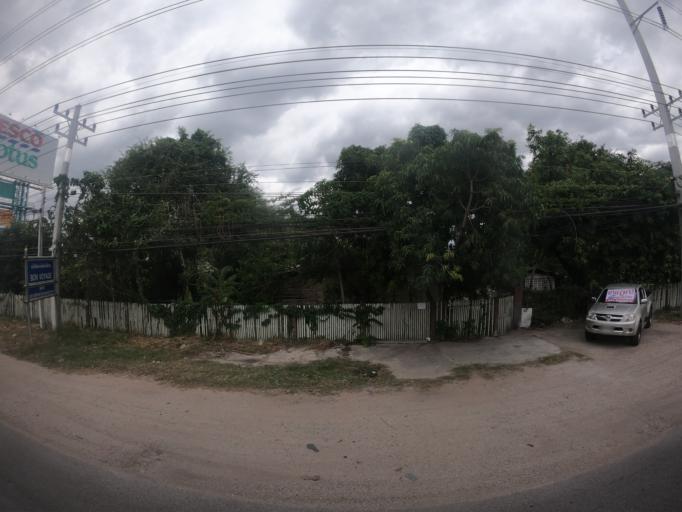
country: TH
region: Nakhon Ratchasima
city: Nakhon Ratchasima
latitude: 14.9483
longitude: 102.1260
